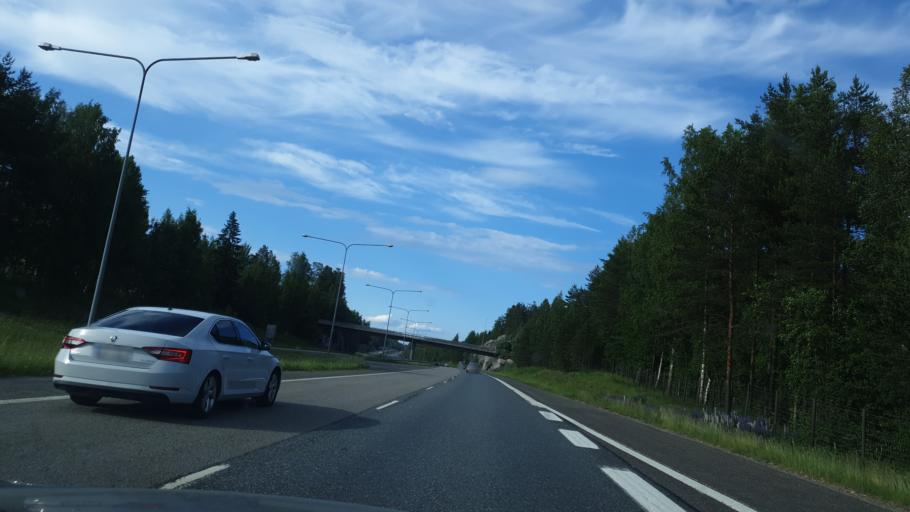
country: FI
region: Paijanne Tavastia
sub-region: Lahti
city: Heinola
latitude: 61.2396
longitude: 26.0481
